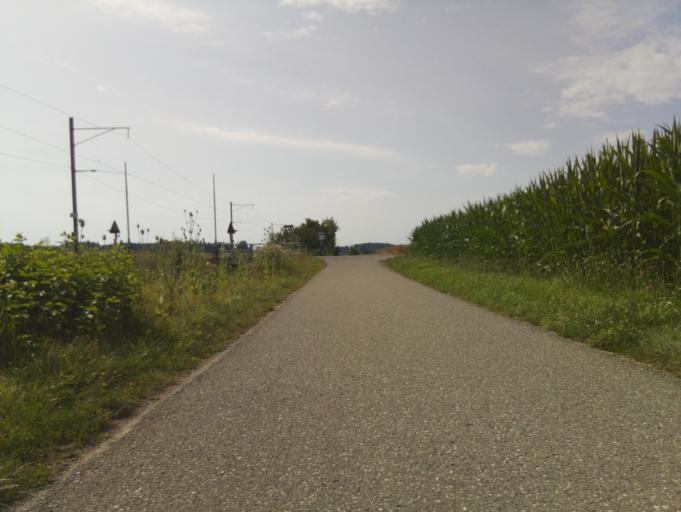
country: CH
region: Zurich
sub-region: Bezirk Andelfingen
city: Henggart
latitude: 47.5749
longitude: 8.6810
